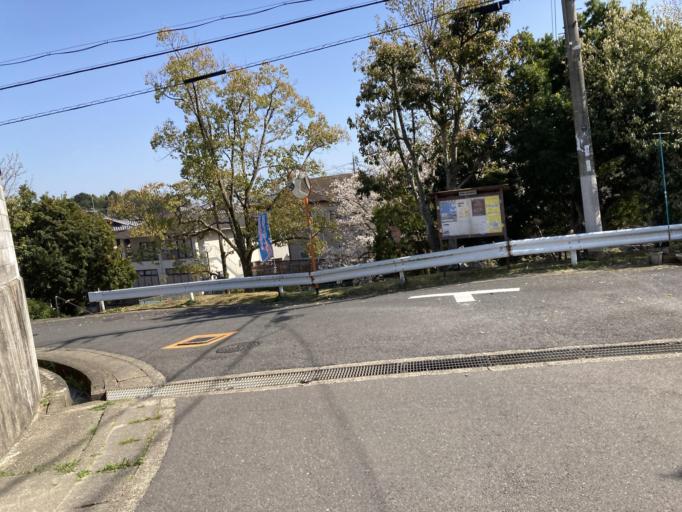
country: JP
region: Nara
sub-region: Ikoma-shi
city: Ikoma
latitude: 34.7079
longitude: 135.6914
